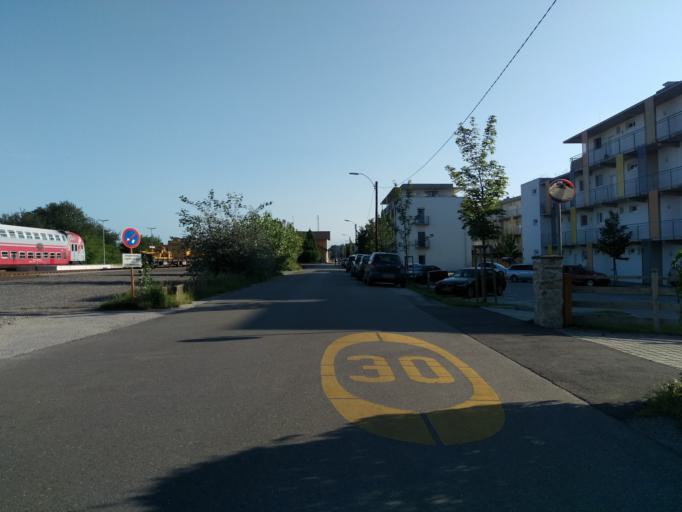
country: AT
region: Styria
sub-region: Politischer Bezirk Graz-Umgebung
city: Seiersberg
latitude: 47.0216
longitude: 15.4054
